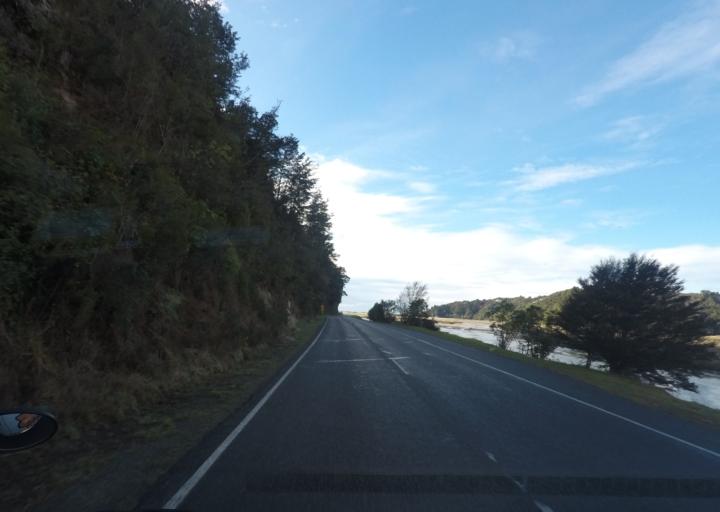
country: NZ
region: Tasman
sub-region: Tasman District
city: Motueka
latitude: -41.0145
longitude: 172.9951
